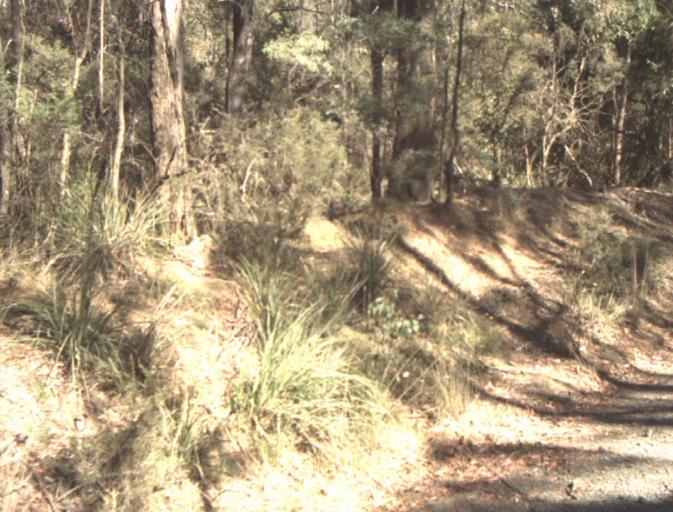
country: AU
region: Tasmania
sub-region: Launceston
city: Newstead
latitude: -41.3606
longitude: 147.2282
